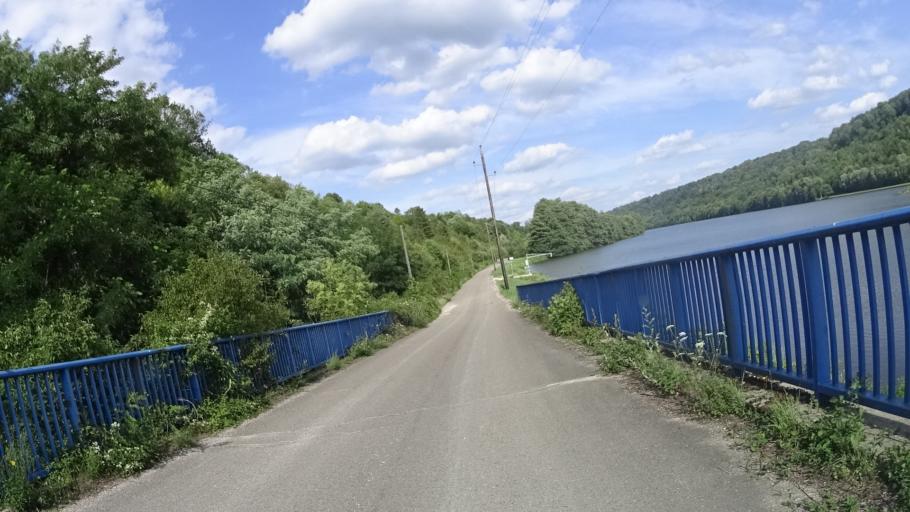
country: FR
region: Lorraine
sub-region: Departement de Meurthe-et-Moselle
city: Gondreville
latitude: 48.6522
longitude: 5.9781
